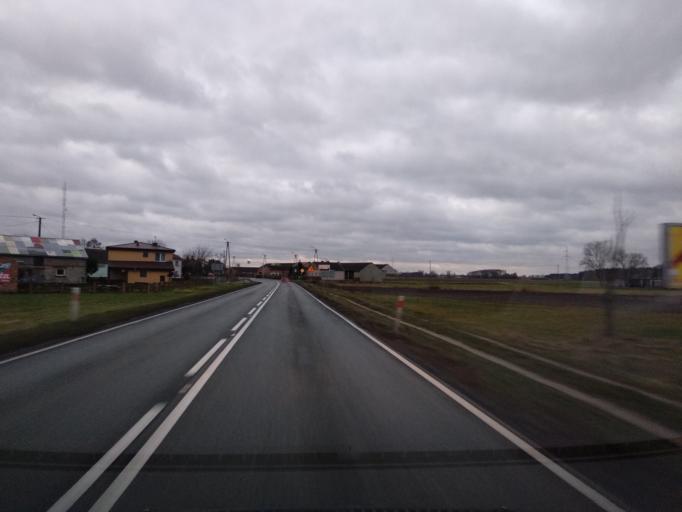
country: PL
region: Greater Poland Voivodeship
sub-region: Powiat koninski
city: Rychwal
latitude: 52.1239
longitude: 18.1723
